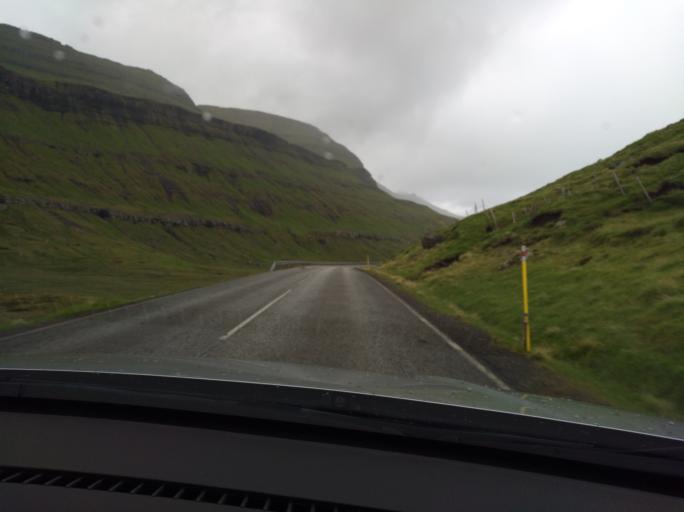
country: FO
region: Eysturoy
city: Fuglafjordur
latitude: 62.2314
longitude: -6.8801
